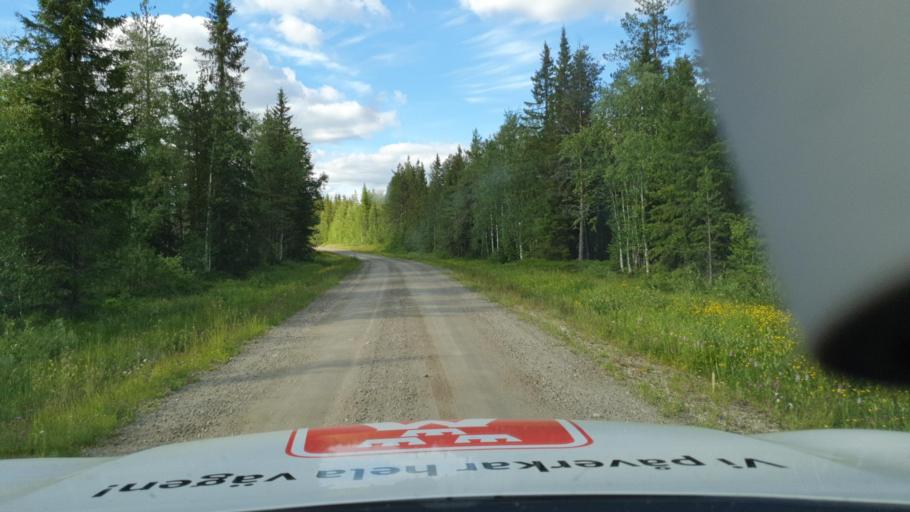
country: SE
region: Vaesterbotten
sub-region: Lycksele Kommun
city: Lycksele
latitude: 64.4772
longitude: 18.2858
